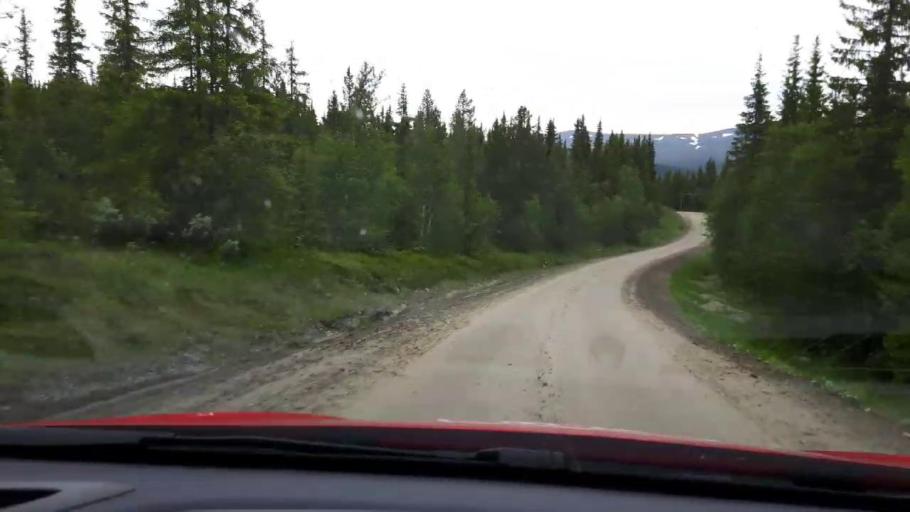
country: SE
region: Jaemtland
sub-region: Are Kommun
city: Are
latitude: 62.8478
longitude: 12.7885
